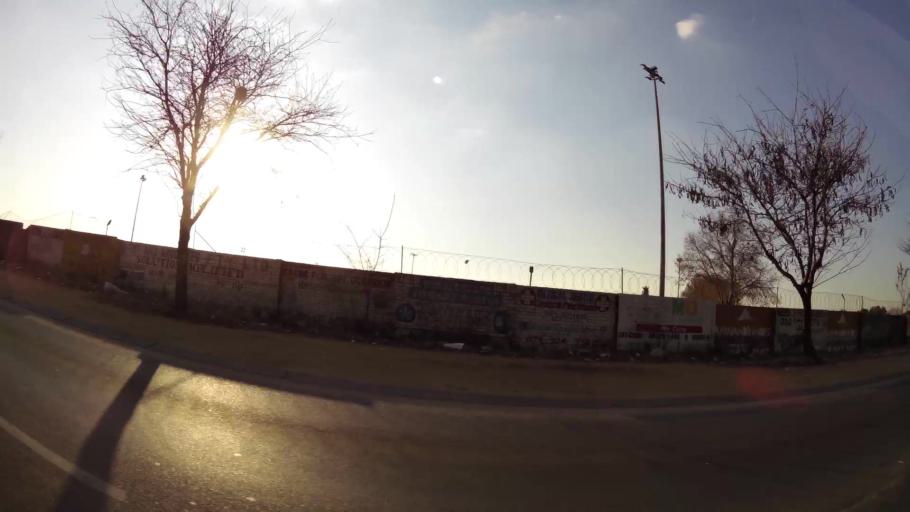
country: ZA
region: Gauteng
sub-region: City of Johannesburg Metropolitan Municipality
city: Midrand
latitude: -26.0223
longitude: 28.1699
